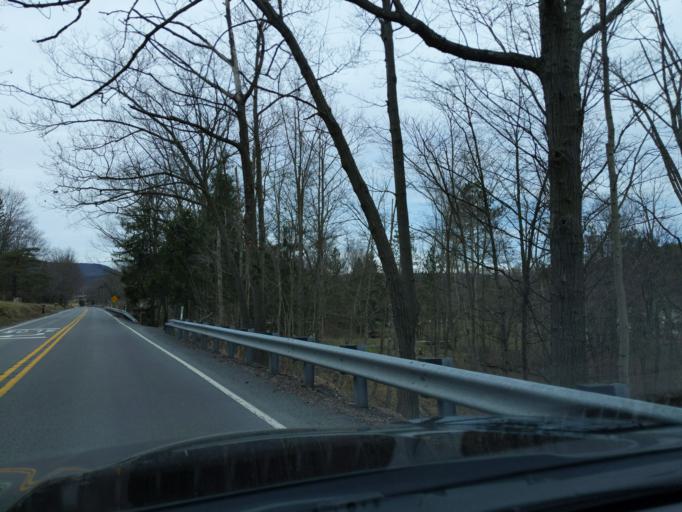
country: US
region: Pennsylvania
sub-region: Blair County
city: Greenwood
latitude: 40.5565
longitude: -78.3737
